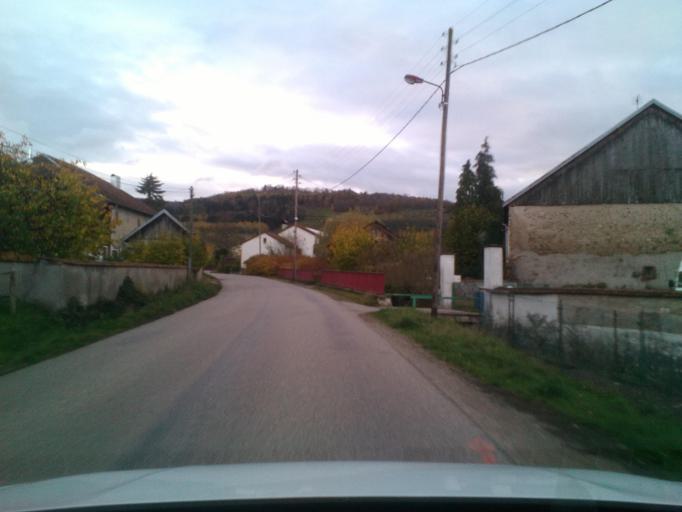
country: FR
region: Lorraine
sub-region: Departement des Vosges
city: Ban-de-Laveline
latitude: 48.2340
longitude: 7.0610
